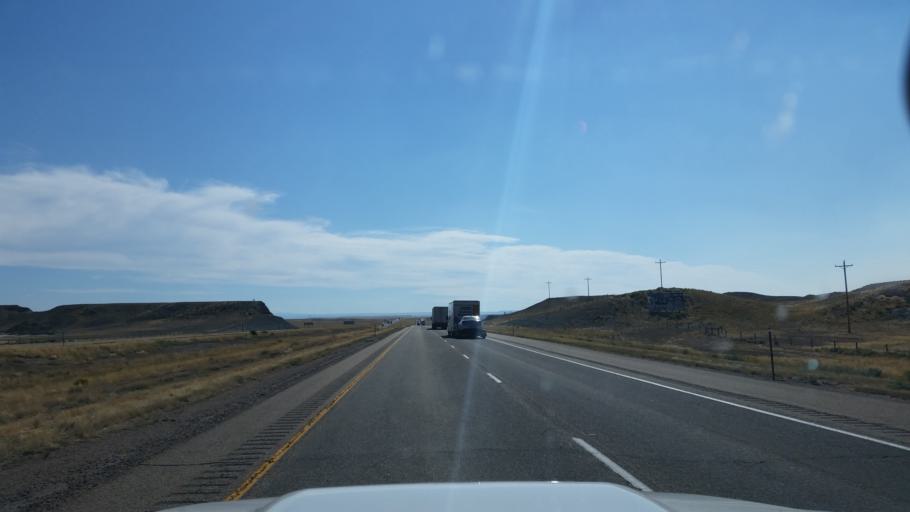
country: US
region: Wyoming
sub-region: Uinta County
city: Lyman
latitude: 41.4038
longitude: -110.1627
